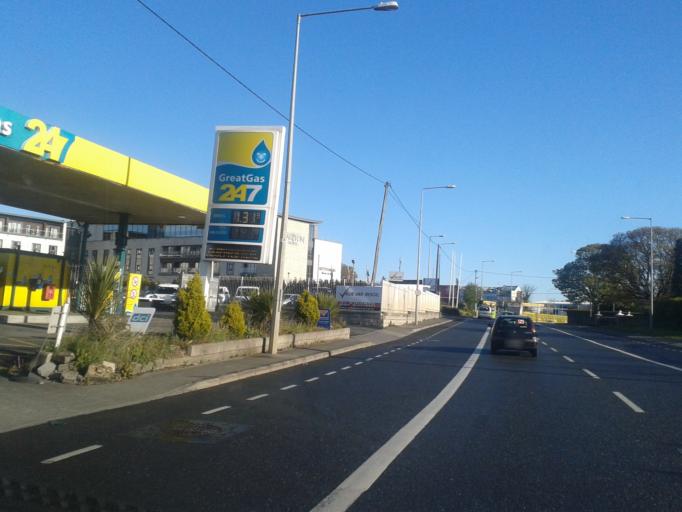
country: IE
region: Leinster
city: Beaumont
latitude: 53.4143
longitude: -6.2390
